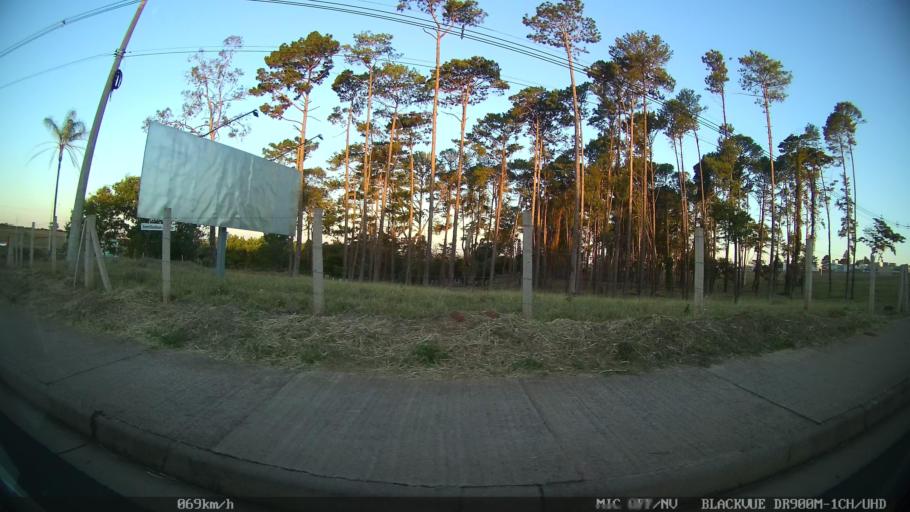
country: BR
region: Sao Paulo
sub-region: Sao Jose Do Rio Preto
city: Sao Jose do Rio Preto
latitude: -20.8576
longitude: -49.4061
